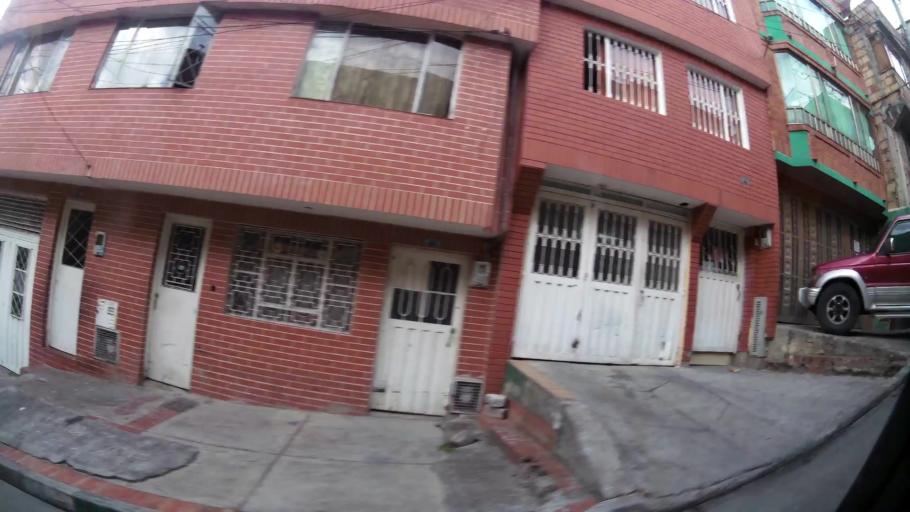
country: CO
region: Bogota D.C.
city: Barrio San Luis
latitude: 4.7215
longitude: -74.0869
